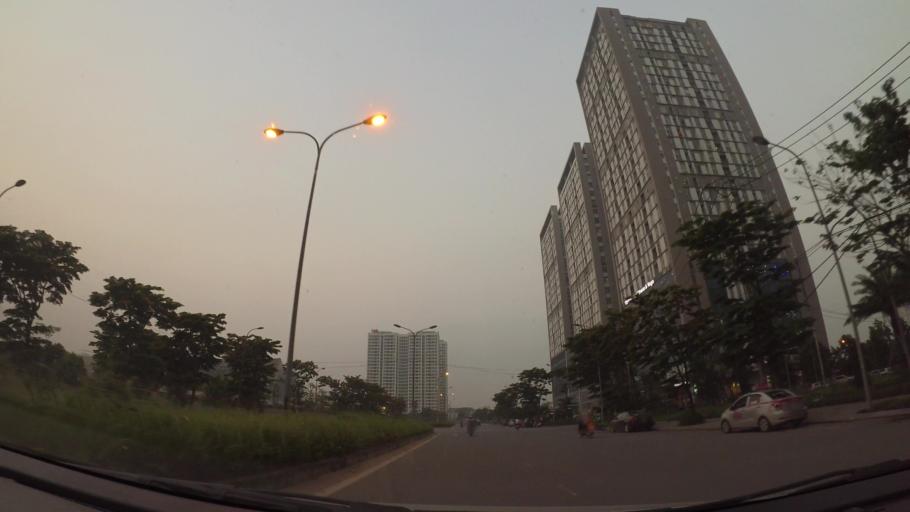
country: VN
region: Ha Noi
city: Tay Ho
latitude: 21.0655
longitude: 105.7977
